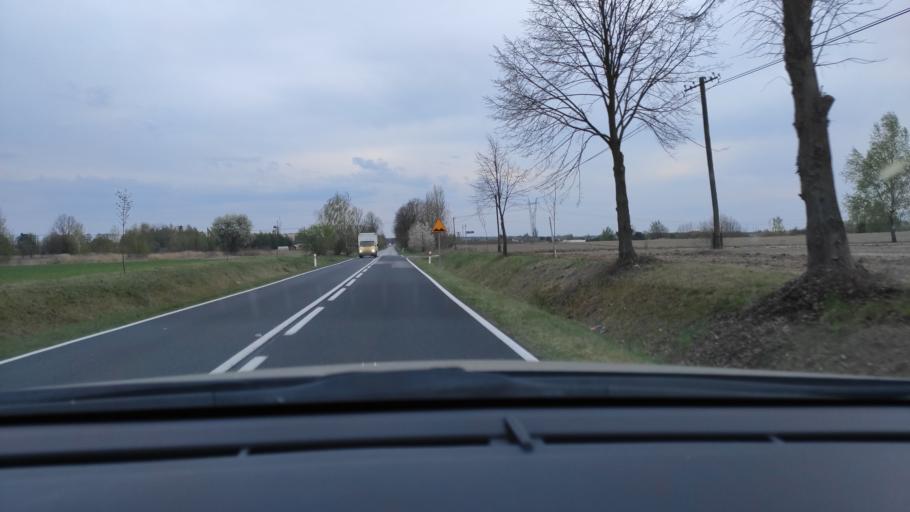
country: PL
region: Masovian Voivodeship
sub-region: Powiat zwolenski
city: Zwolen
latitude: 51.3701
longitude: 21.5637
